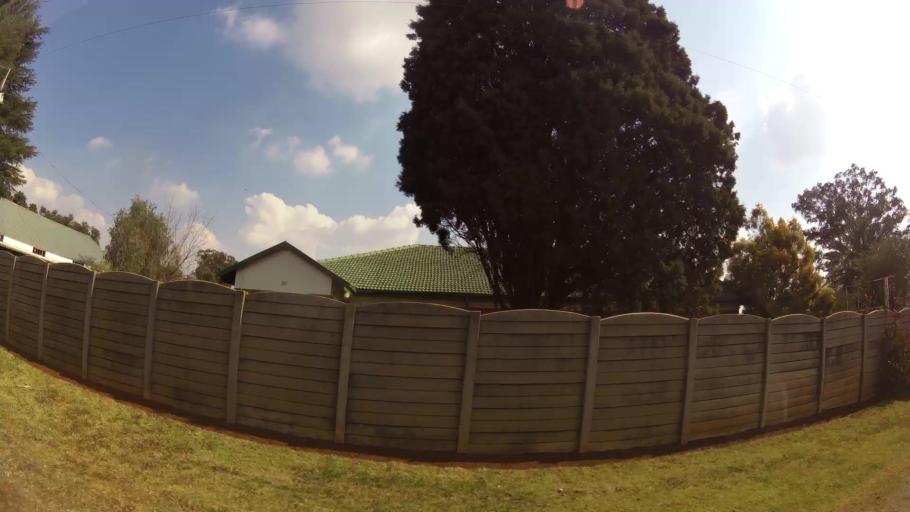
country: ZA
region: Mpumalanga
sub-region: Nkangala District Municipality
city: Delmas
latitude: -26.1806
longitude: 28.5405
